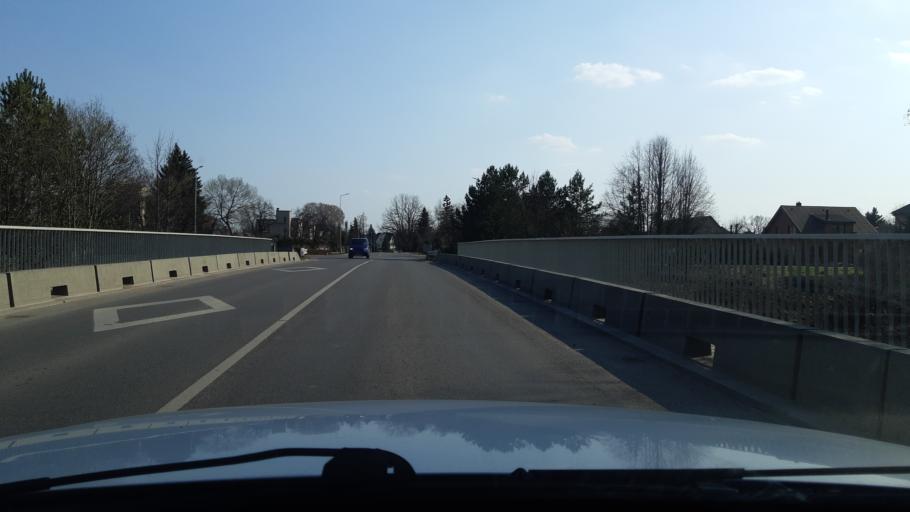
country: LT
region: Kauno apskritis
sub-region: Kaunas
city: Aleksotas
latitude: 54.8399
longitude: 23.9475
